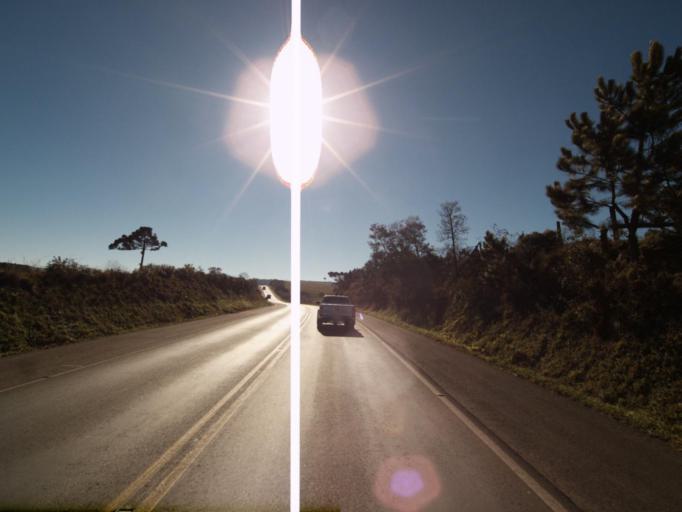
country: BR
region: Santa Catarina
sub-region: Concordia
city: Concordia
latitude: -26.9154
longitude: -51.9207
